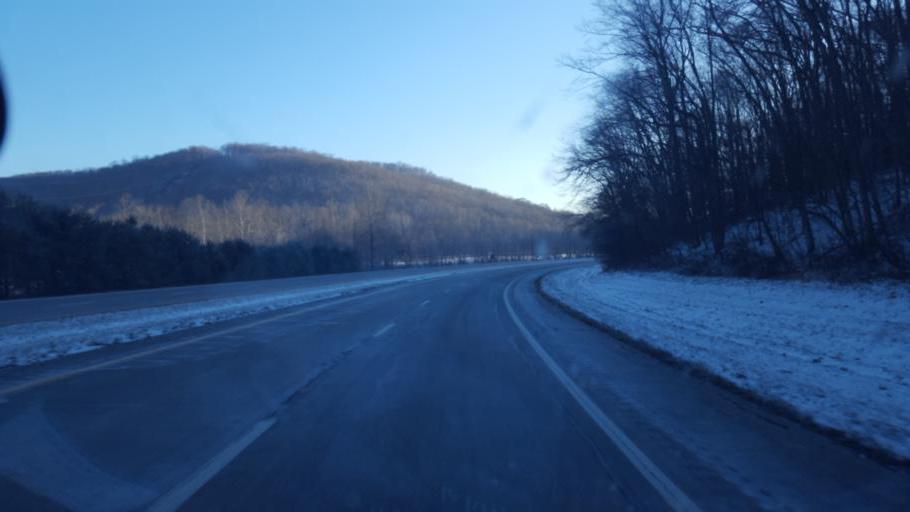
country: US
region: Ohio
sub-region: Adams County
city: Peebles
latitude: 39.0370
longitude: -83.2570
